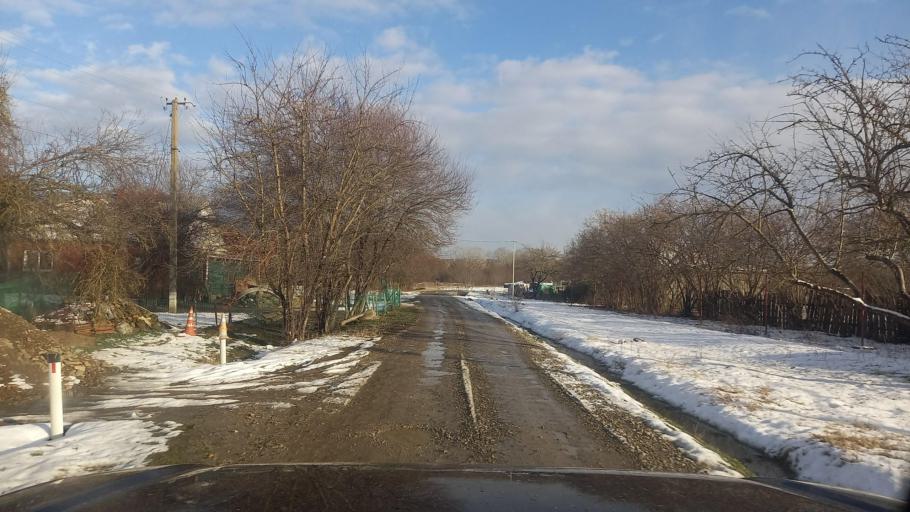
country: RU
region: Krasnodarskiy
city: Smolenskaya
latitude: 44.7761
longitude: 38.8490
